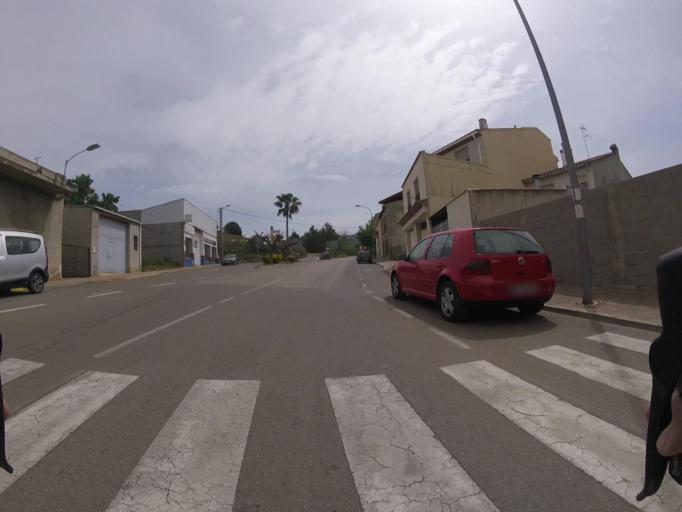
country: ES
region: Valencia
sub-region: Provincia de Castello
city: Cabanes
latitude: 40.1544
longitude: 0.0482
